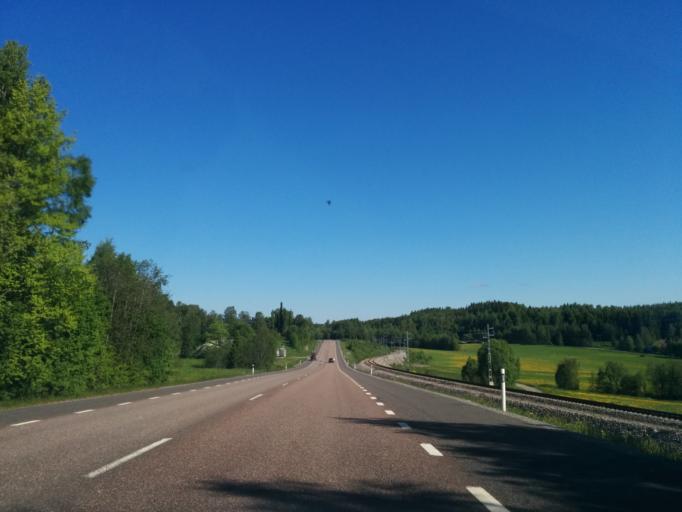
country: SE
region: Vaesternorrland
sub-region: Kramfors Kommun
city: Kramfors
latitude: 62.8911
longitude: 17.8519
